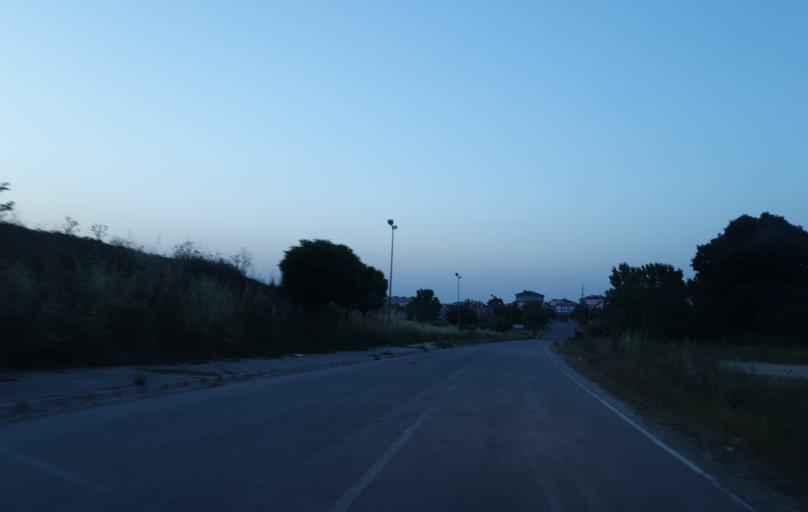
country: TR
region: Tekirdag
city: Saray
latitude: 41.3671
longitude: 27.9286
